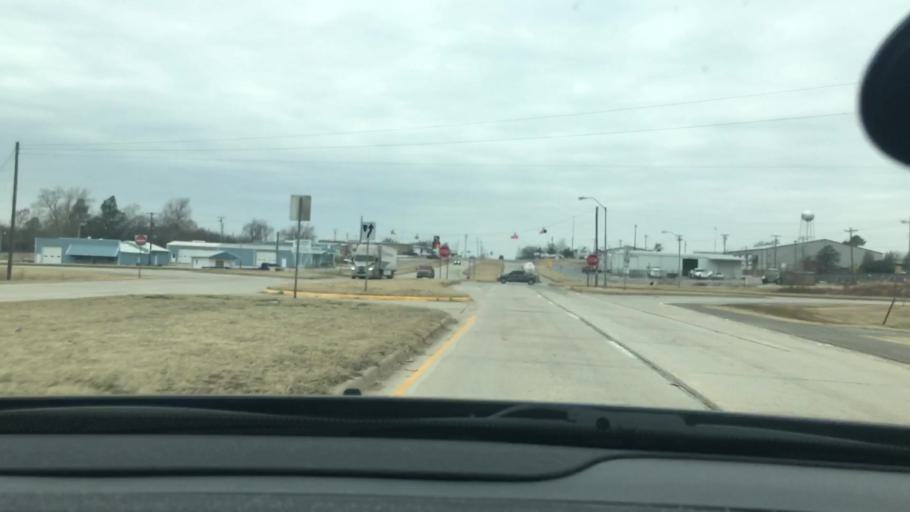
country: US
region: Oklahoma
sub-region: Carter County
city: Healdton
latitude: 34.4489
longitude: -97.5084
